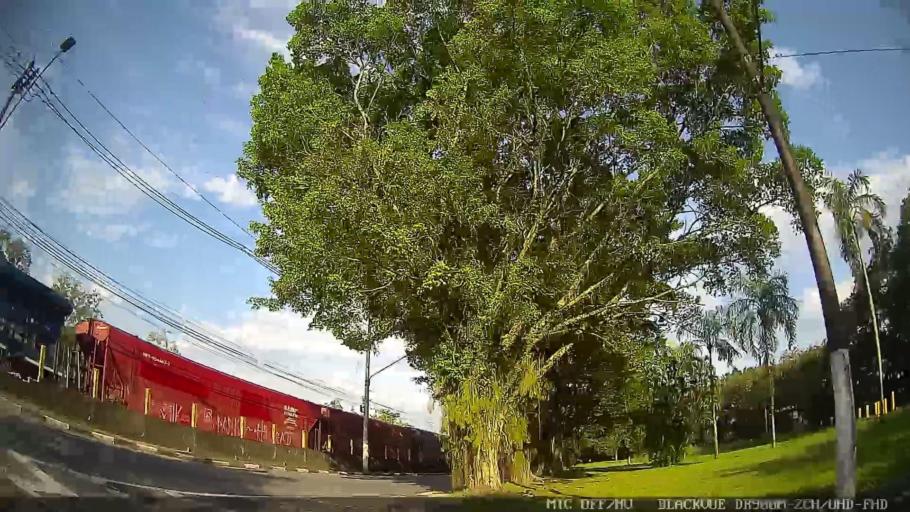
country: BR
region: Sao Paulo
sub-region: Cubatao
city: Cubatao
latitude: -23.9146
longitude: -46.4195
